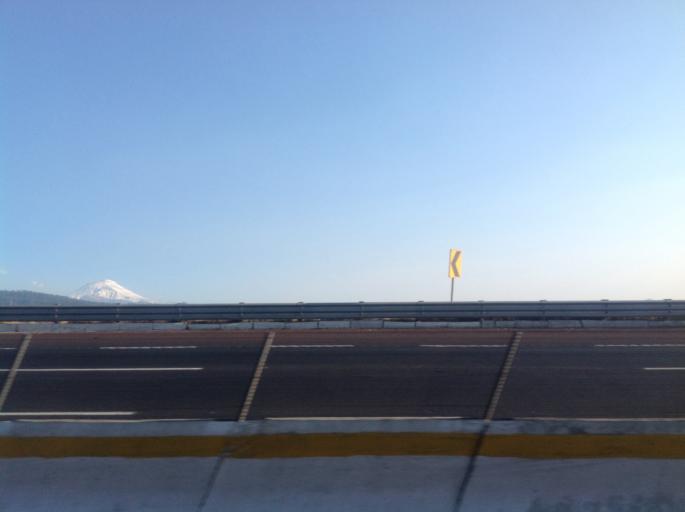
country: MX
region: Mexico
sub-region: Ixtapaluca
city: San Jeronimo Cuatro Vientos
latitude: 19.2978
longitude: -98.7733
